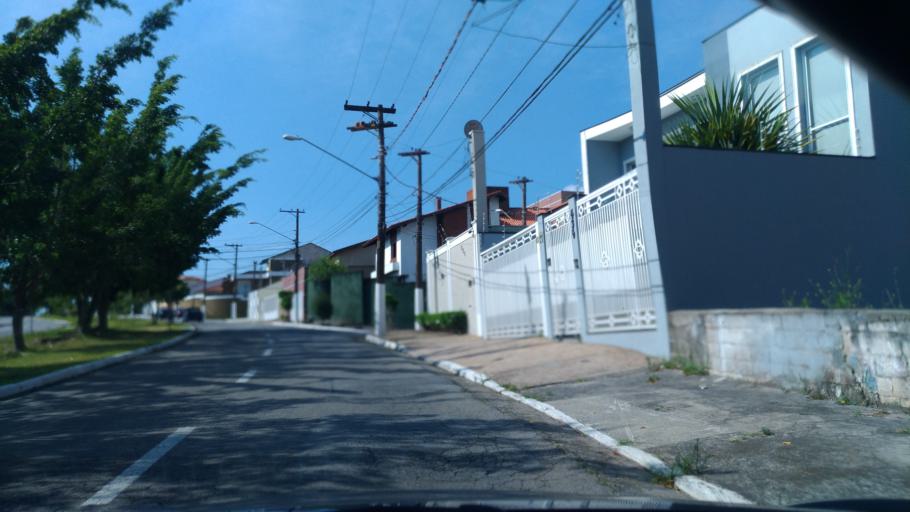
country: BR
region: Sao Paulo
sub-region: Sao Bernardo Do Campo
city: Sao Bernardo do Campo
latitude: -23.7105
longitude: -46.5790
